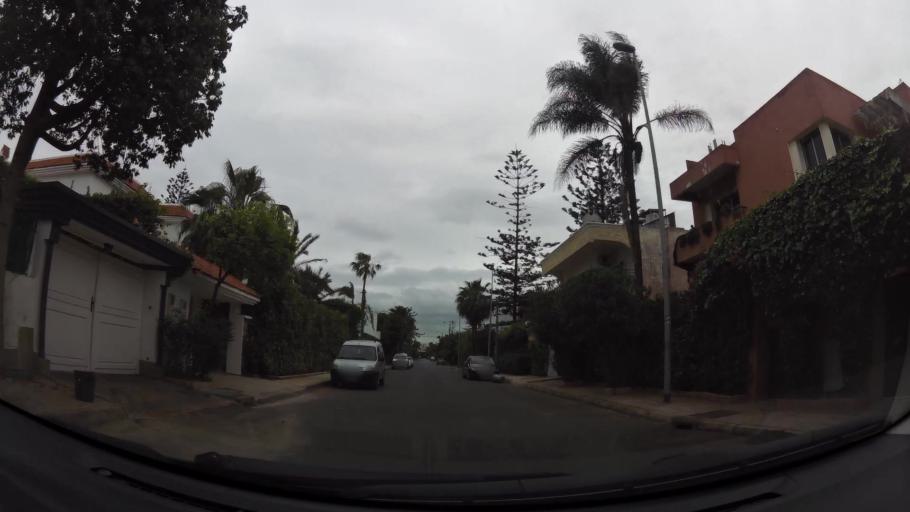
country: MA
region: Grand Casablanca
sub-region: Casablanca
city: Casablanca
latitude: 33.5831
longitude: -7.6565
